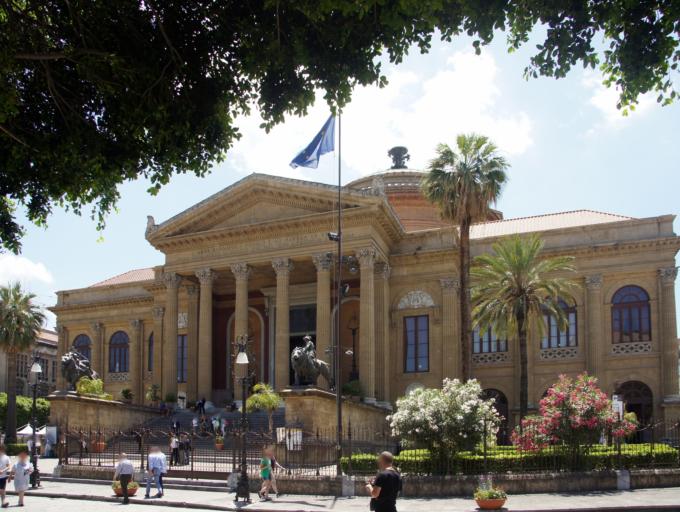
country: IT
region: Sicily
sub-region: Palermo
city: Palermo
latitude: 38.1211
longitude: 13.3578
